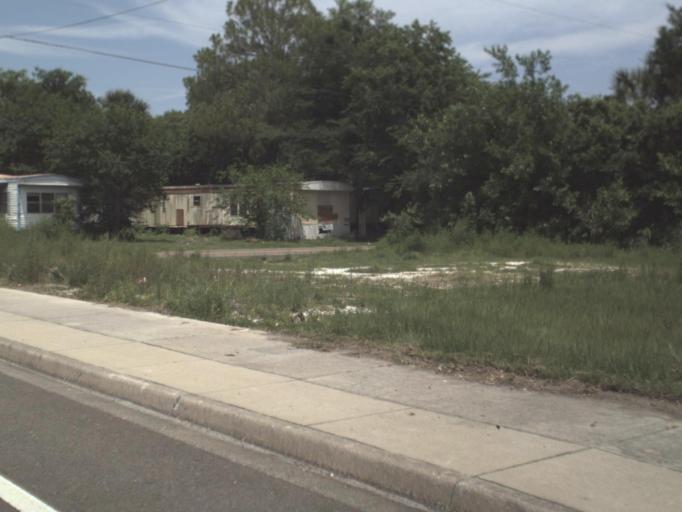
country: US
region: Florida
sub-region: Duval County
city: Jacksonville
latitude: 30.3691
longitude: -81.6519
